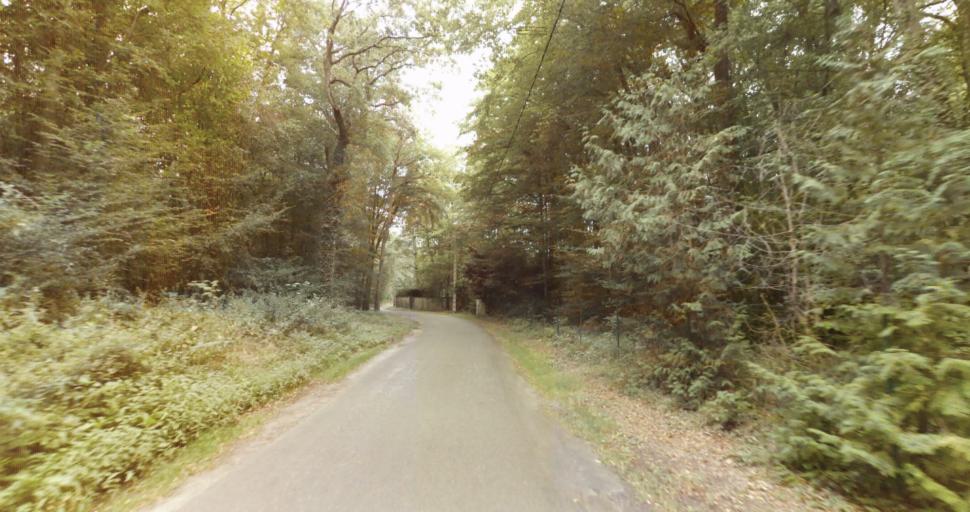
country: FR
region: Haute-Normandie
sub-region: Departement de l'Eure
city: La Couture-Boussey
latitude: 48.9003
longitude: 1.3635
